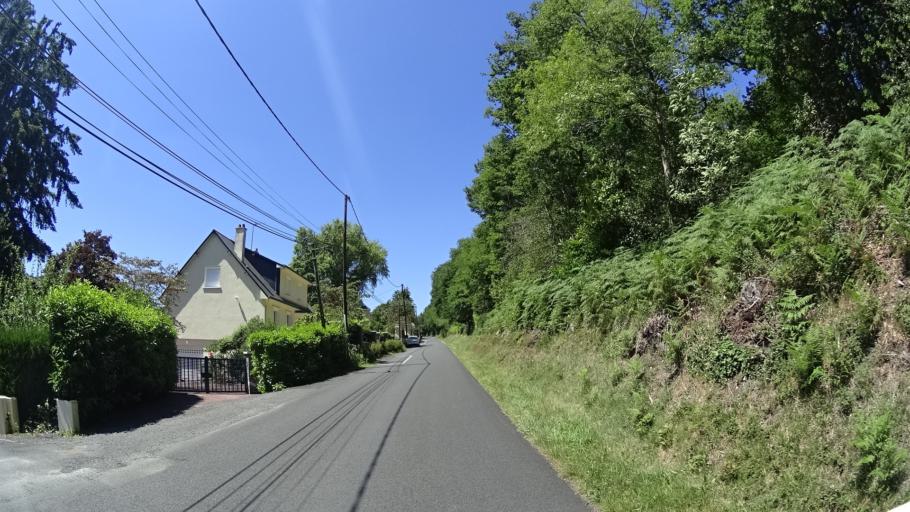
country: FR
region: Pays de la Loire
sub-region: Departement de Maine-et-Loire
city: Saint-Martin-de-la-Place
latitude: 47.2798
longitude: -0.1255
